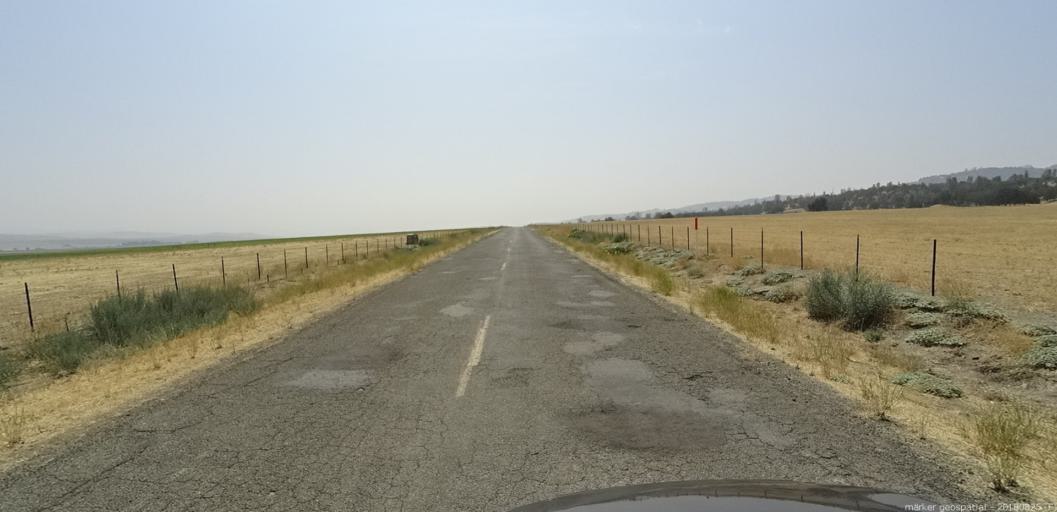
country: US
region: California
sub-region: San Luis Obispo County
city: Shandon
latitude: 35.8182
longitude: -120.3794
